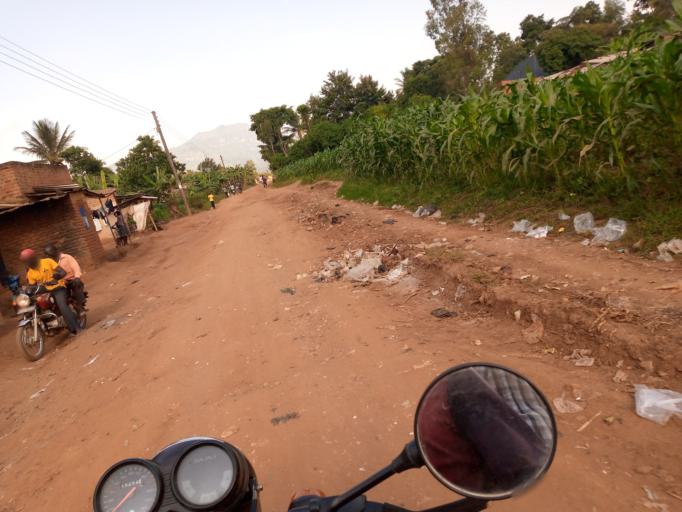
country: UG
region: Eastern Region
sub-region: Mbale District
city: Mbale
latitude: 1.0543
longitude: 34.1649
